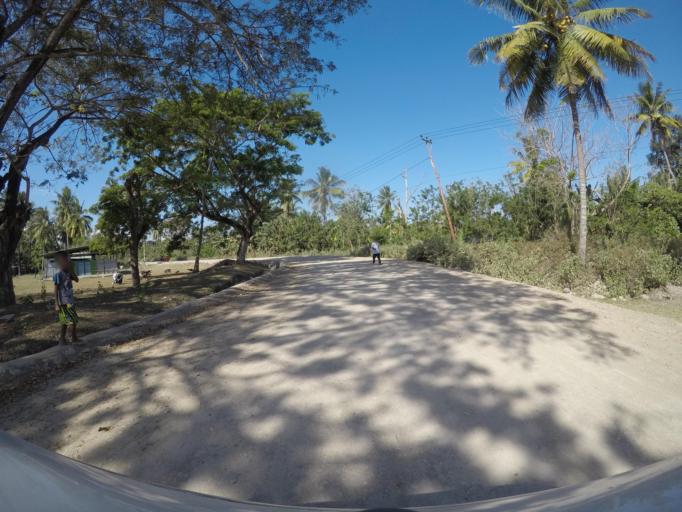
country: TL
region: Viqueque
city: Viqueque
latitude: -8.8599
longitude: 126.5091
